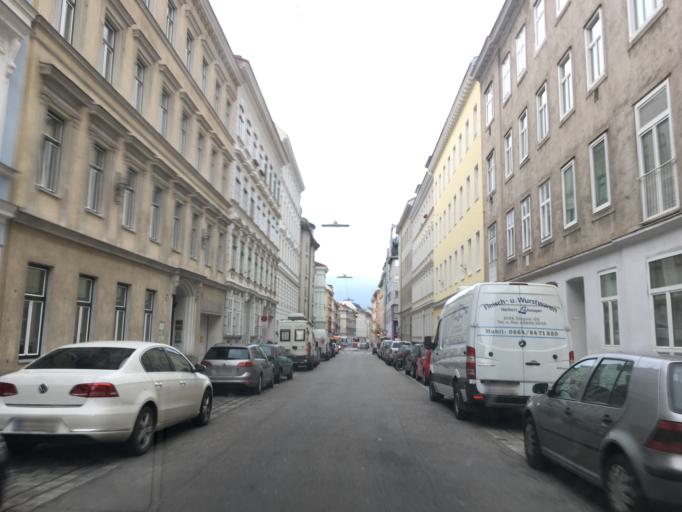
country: AT
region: Vienna
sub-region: Wien Stadt
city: Vienna
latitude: 48.1873
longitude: 16.3578
